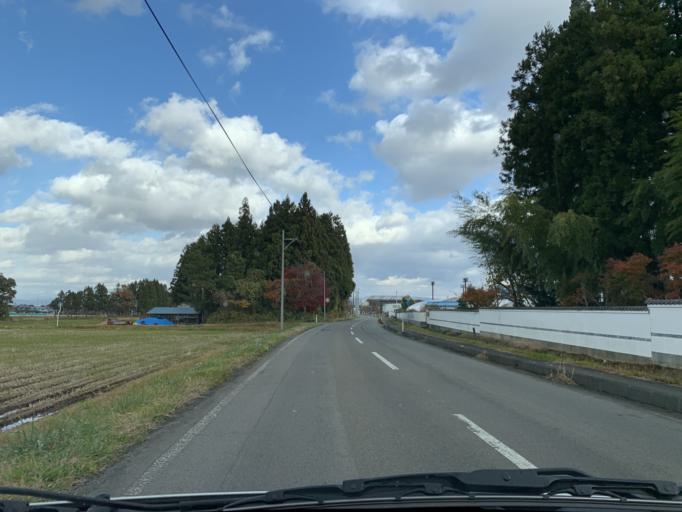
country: JP
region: Iwate
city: Mizusawa
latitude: 39.1209
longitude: 141.0623
